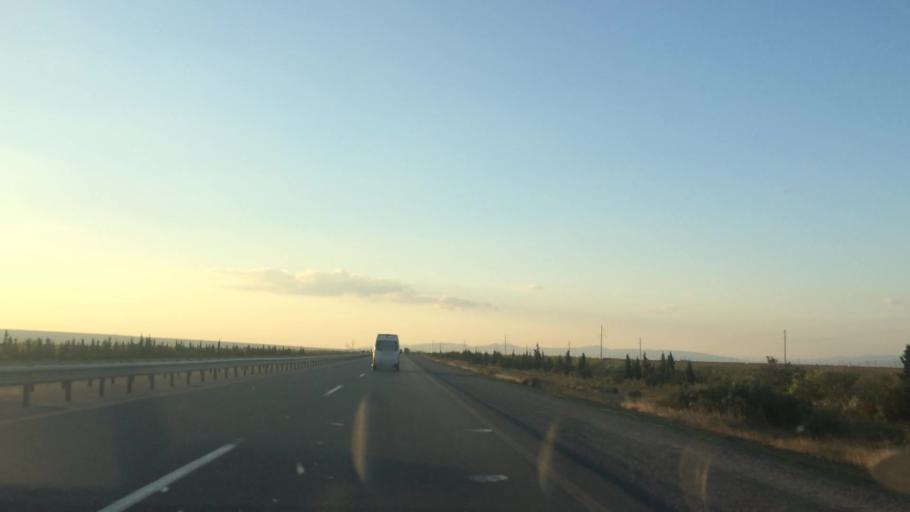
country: AZ
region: Baki
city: Qobustan
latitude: 39.9919
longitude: 49.1945
